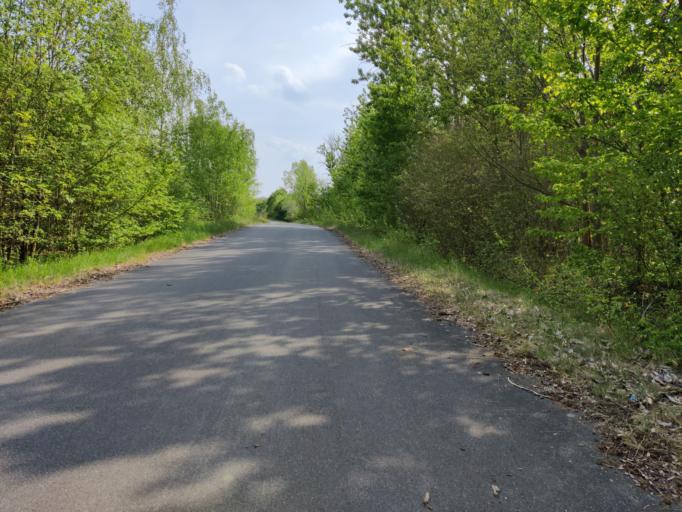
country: DE
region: Saxony
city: Markkleeberg
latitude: 51.2439
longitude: 12.3667
